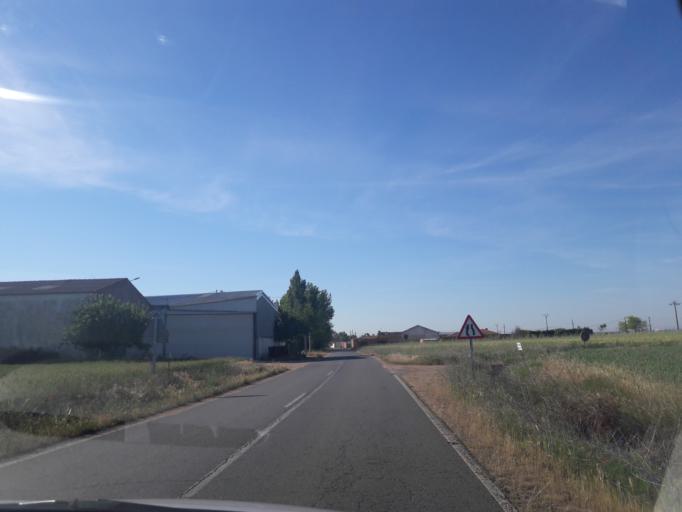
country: ES
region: Castille and Leon
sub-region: Provincia de Salamanca
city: Arcediano
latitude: 41.0958
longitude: -5.5627
